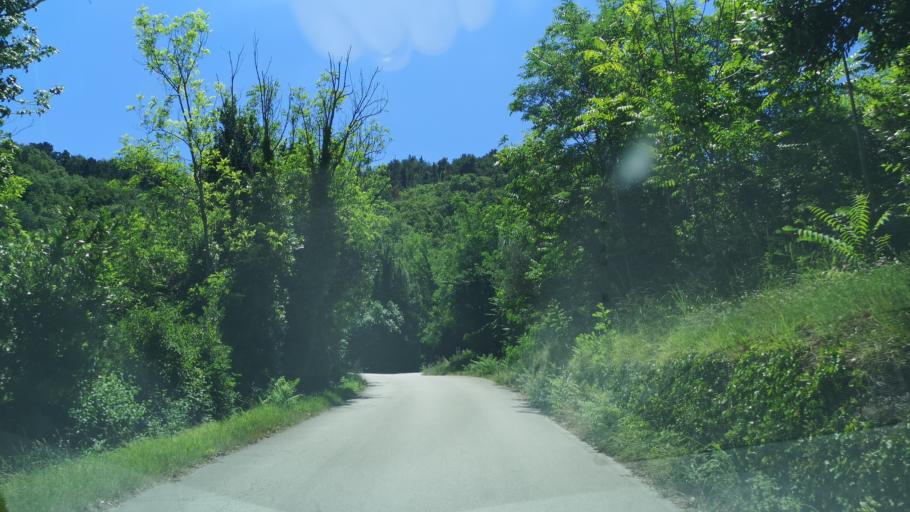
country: SI
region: Piran-Pirano
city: Portoroz
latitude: 45.5238
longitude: 13.5952
